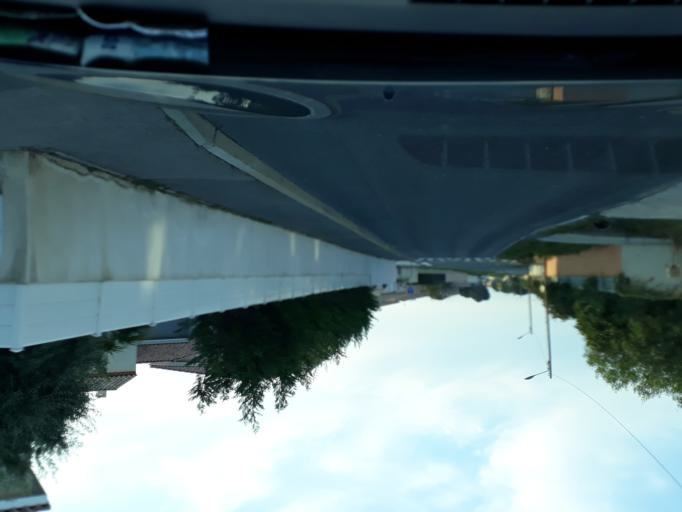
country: FR
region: Languedoc-Roussillon
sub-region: Departement de l'Herault
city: Marseillan
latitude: 43.3404
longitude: 3.5331
